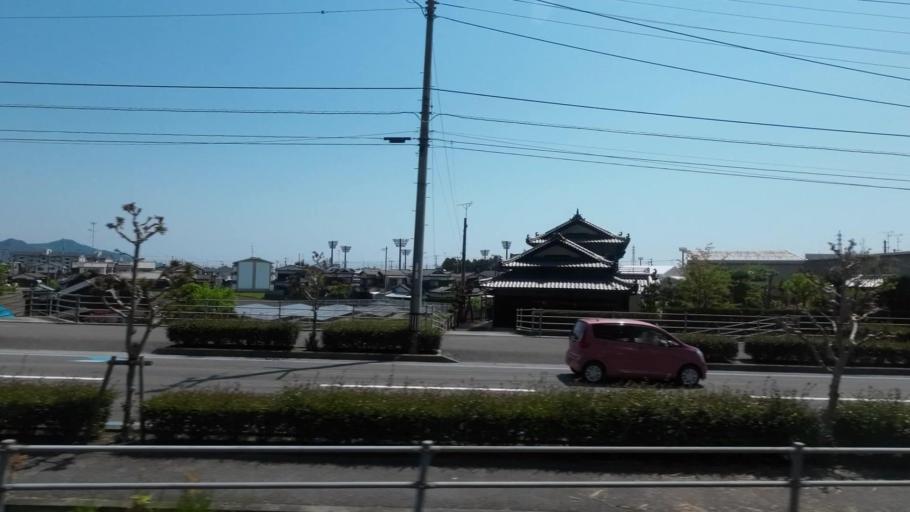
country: JP
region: Ehime
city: Hojo
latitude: 34.0784
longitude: 132.9851
